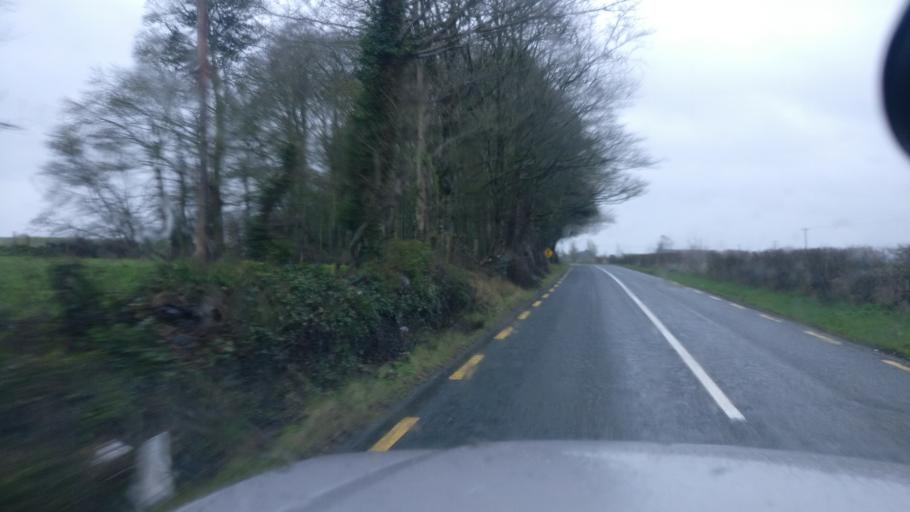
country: IE
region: Connaught
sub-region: County Galway
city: Ballinasloe
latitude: 53.2572
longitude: -8.1825
